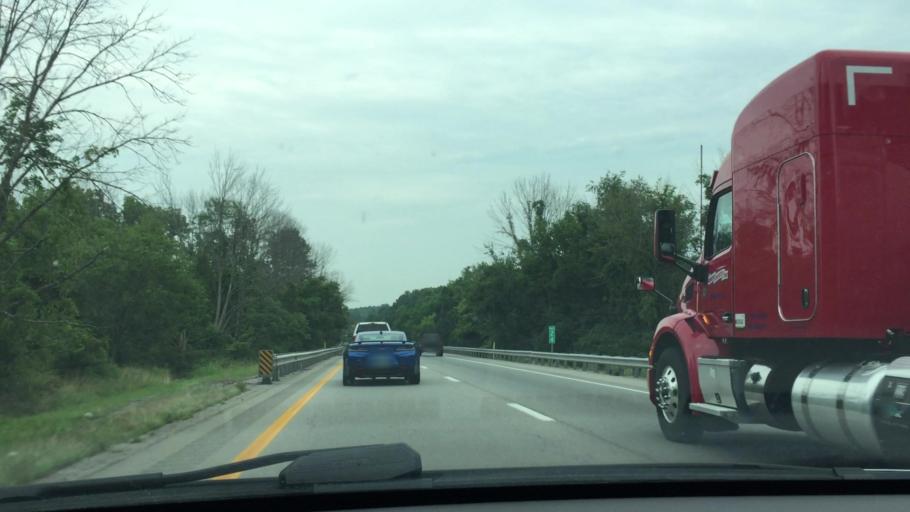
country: US
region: Kentucky
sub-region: Oldham County
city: La Grange
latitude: 38.4157
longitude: -85.3392
